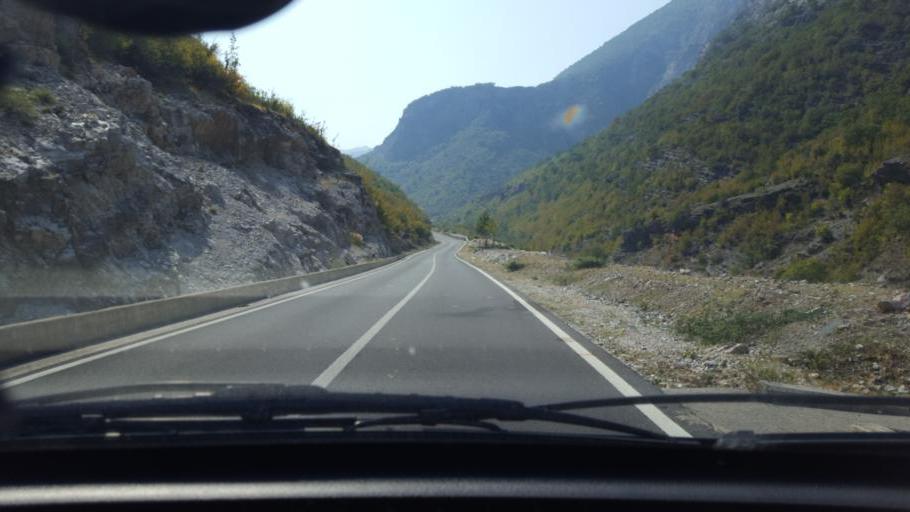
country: AL
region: Shkoder
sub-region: Rrethi i Malesia e Madhe
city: Kastrat
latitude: 42.4495
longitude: 19.5484
